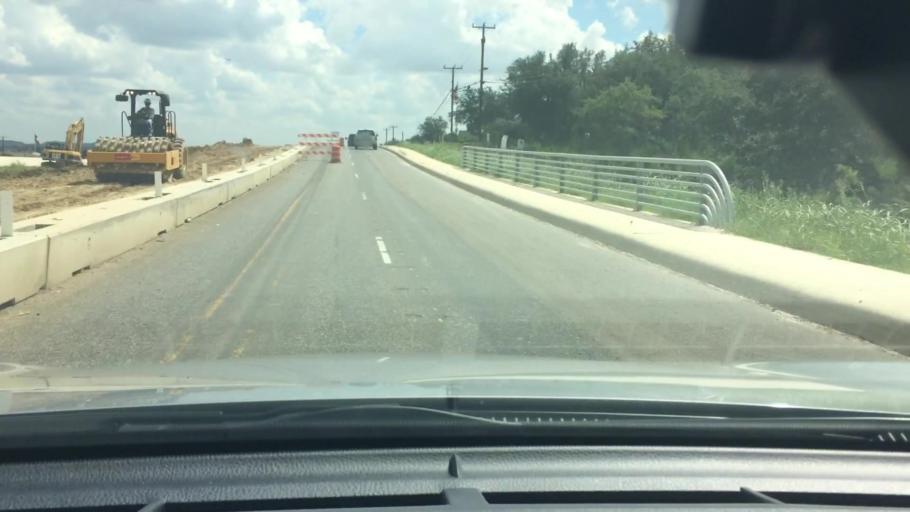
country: US
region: Texas
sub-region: Bexar County
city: Scenic Oaks
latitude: 29.7160
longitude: -98.6637
